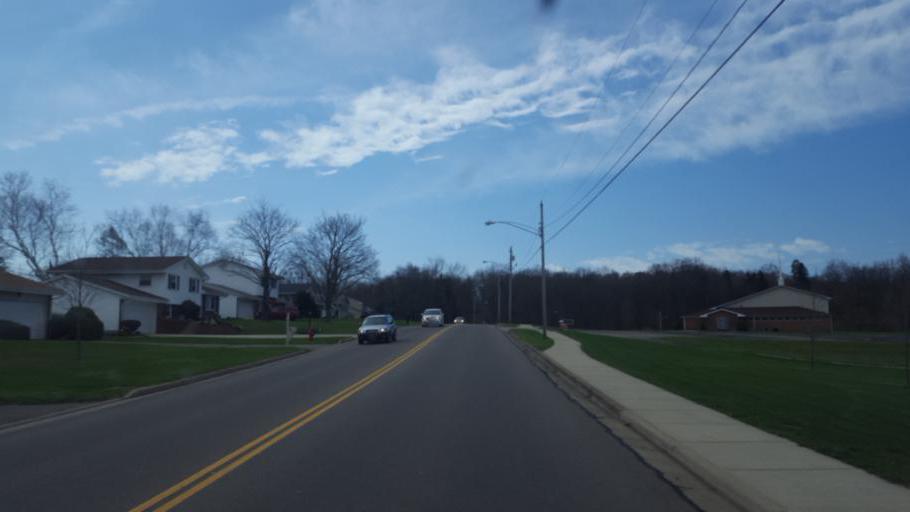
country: US
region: Ohio
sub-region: Knox County
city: Mount Vernon
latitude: 40.3844
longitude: -82.4635
